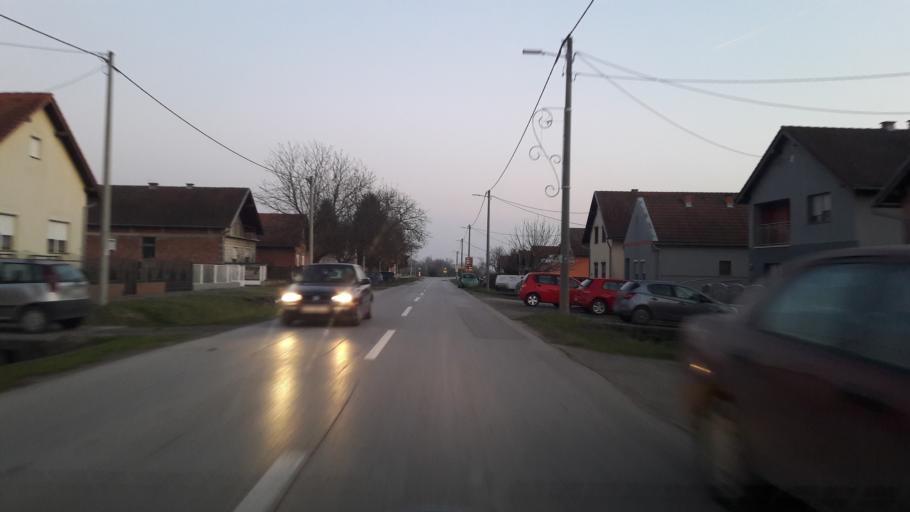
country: HR
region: Vukovarsko-Srijemska
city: Nijemci
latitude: 45.1439
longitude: 19.0356
